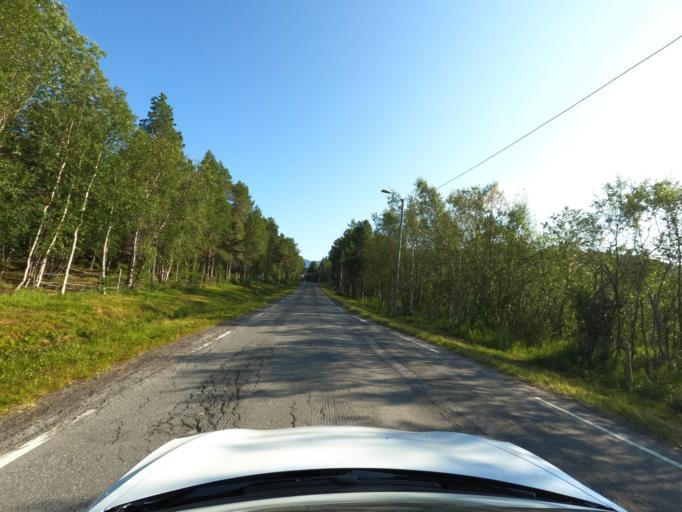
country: NO
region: Nordland
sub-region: Narvik
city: Bjerkvik
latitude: 68.4809
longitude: 17.5275
